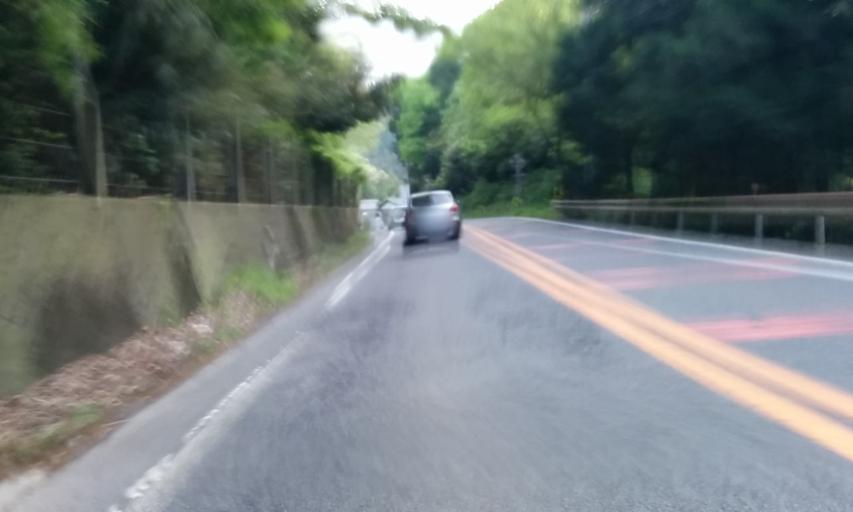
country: JP
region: Ehime
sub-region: Shikoku-chuo Shi
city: Matsuyama
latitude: 33.8216
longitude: 132.9810
